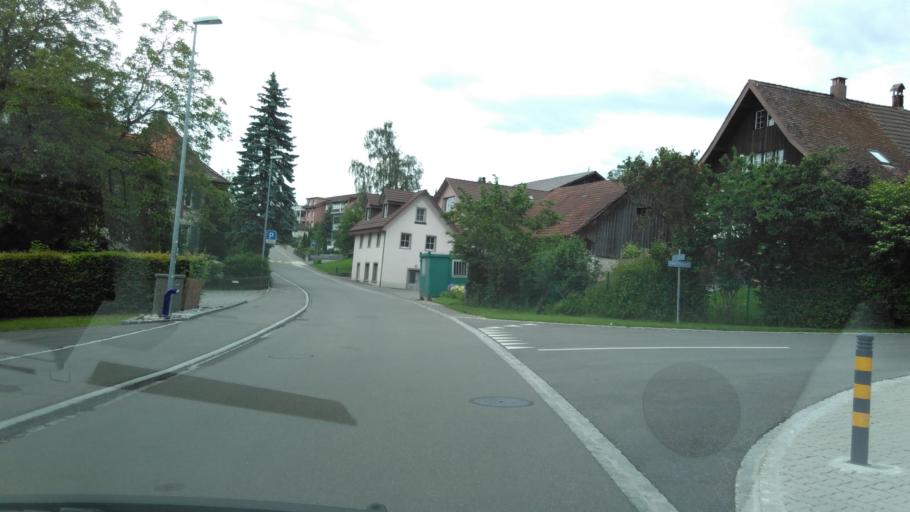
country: CH
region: Aargau
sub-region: Bezirk Baden
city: Kunten
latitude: 47.3905
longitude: 8.3457
